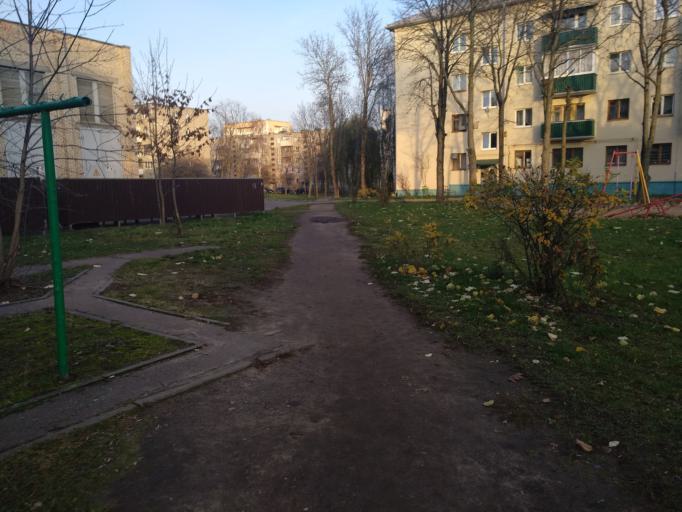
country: BY
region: Minsk
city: Minsk
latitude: 53.9327
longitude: 27.5624
